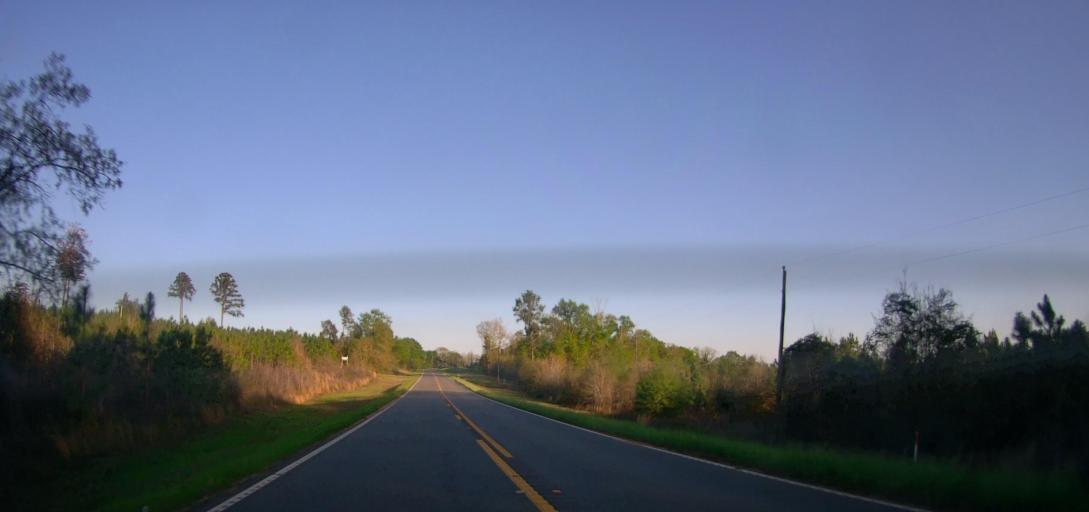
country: US
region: Georgia
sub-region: Marion County
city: Buena Vista
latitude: 32.3741
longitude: -84.4306
